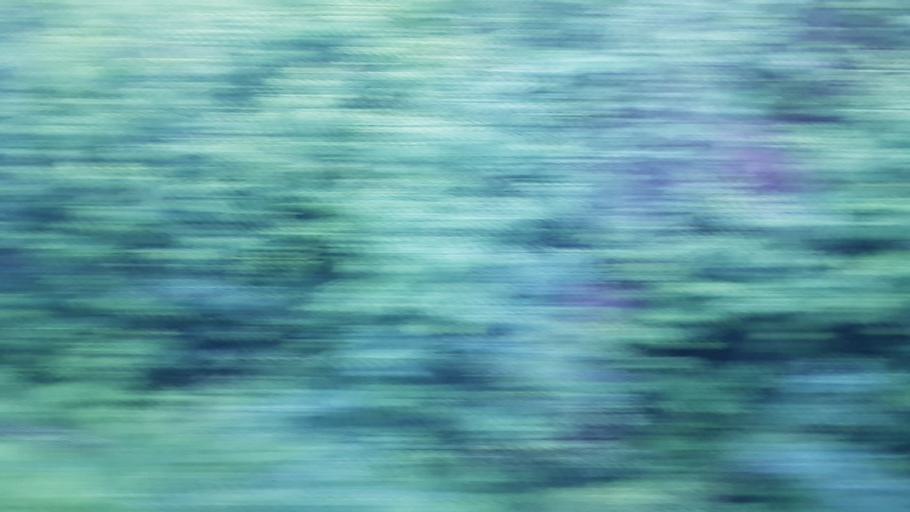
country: NO
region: Sor-Trondelag
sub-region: Melhus
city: Lundamo
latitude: 63.2150
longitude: 10.2975
